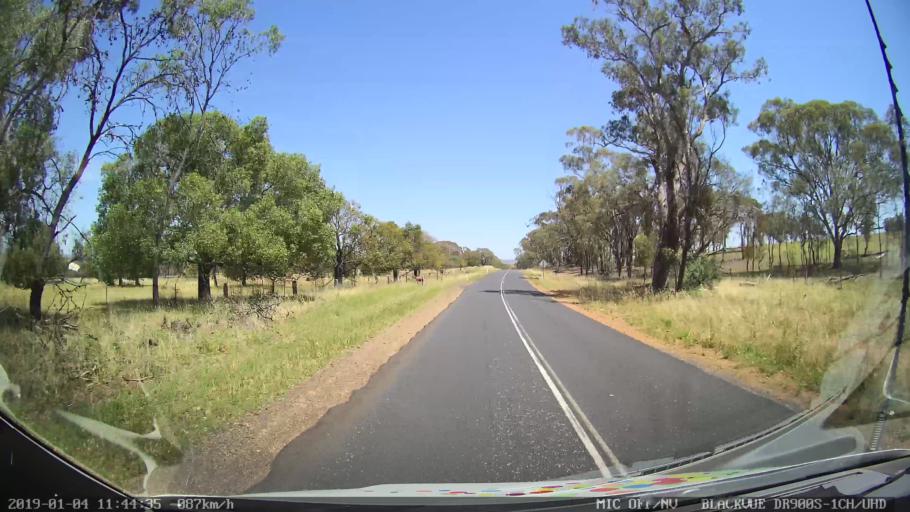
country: AU
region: New South Wales
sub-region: Cabonne
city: Molong
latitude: -32.9625
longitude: 148.7703
